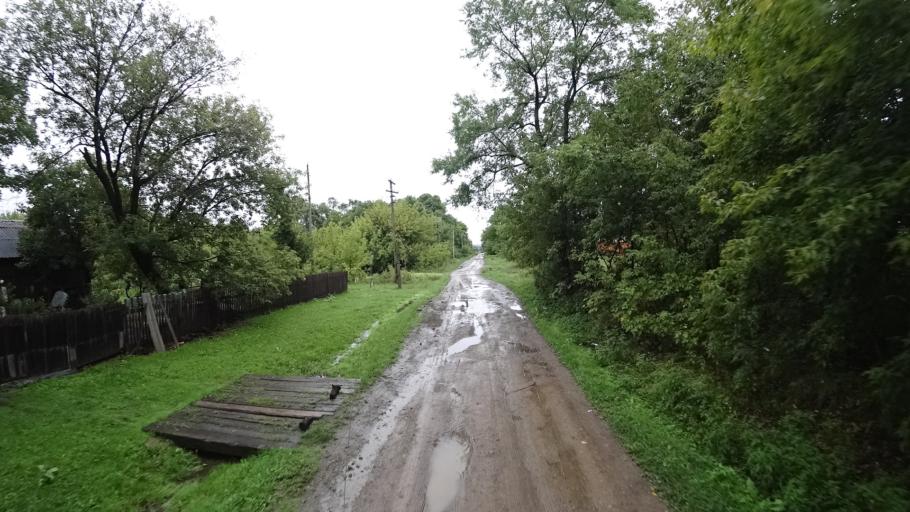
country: RU
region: Primorskiy
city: Monastyrishche
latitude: 44.2529
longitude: 132.4239
